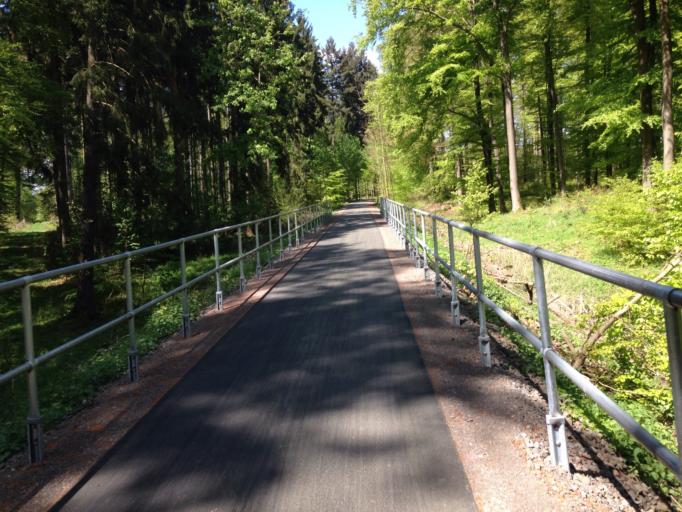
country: DE
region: Hesse
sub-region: Regierungsbezirk Giessen
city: Laubach
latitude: 50.5321
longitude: 8.9495
